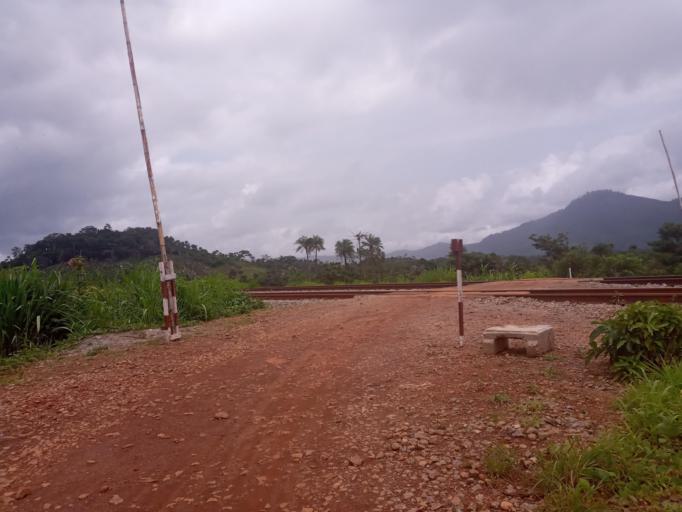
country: SL
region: Northern Province
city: Bumbuna
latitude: 8.9695
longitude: -11.7540
